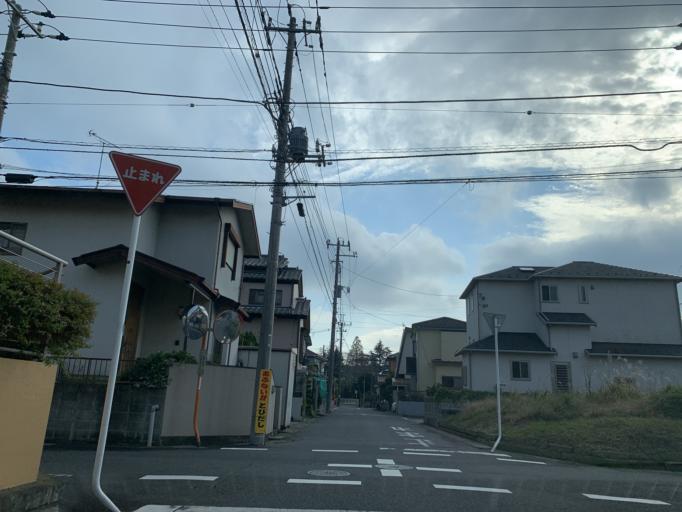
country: JP
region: Chiba
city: Nagareyama
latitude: 35.9099
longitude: 139.9136
